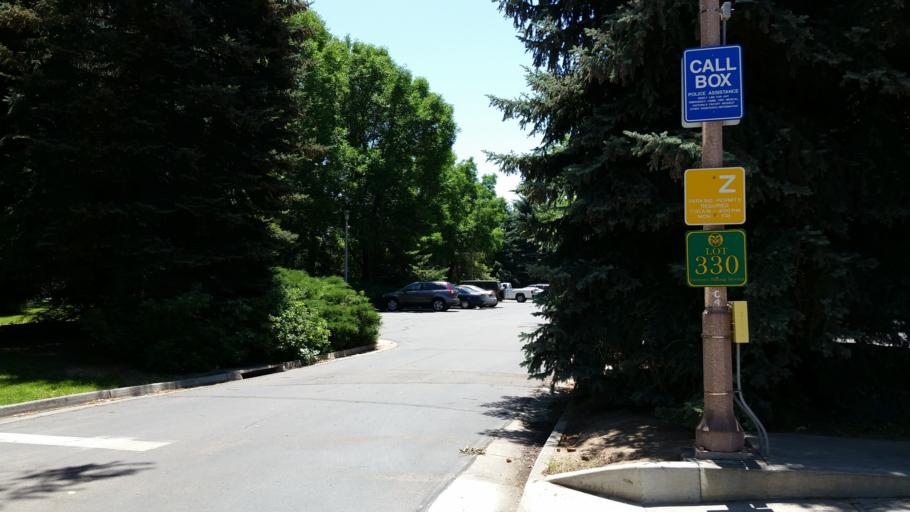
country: US
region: Colorado
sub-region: Larimer County
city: Fort Collins
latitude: 40.5770
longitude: -105.0783
